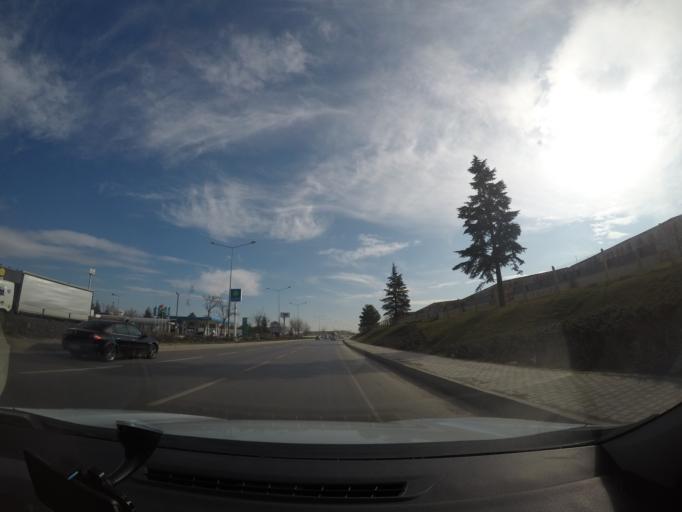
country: TR
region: Eskisehir
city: Eskisehir
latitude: 39.7967
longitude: 30.5205
